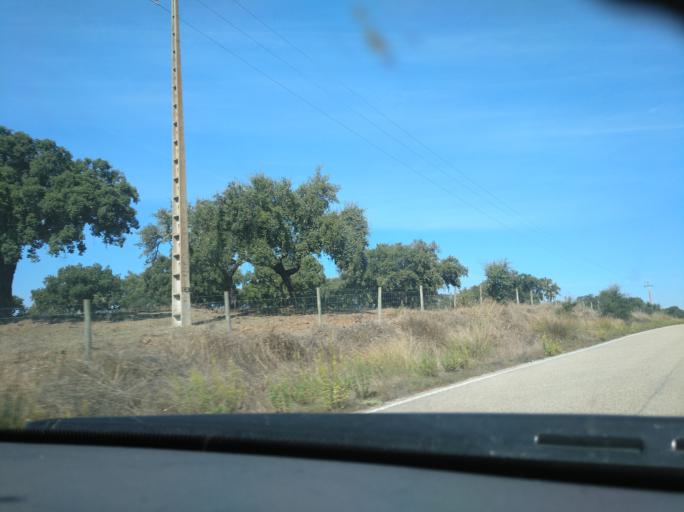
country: PT
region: Evora
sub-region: Arraiolos
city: Arraiolos
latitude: 38.6742
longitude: -8.0946
